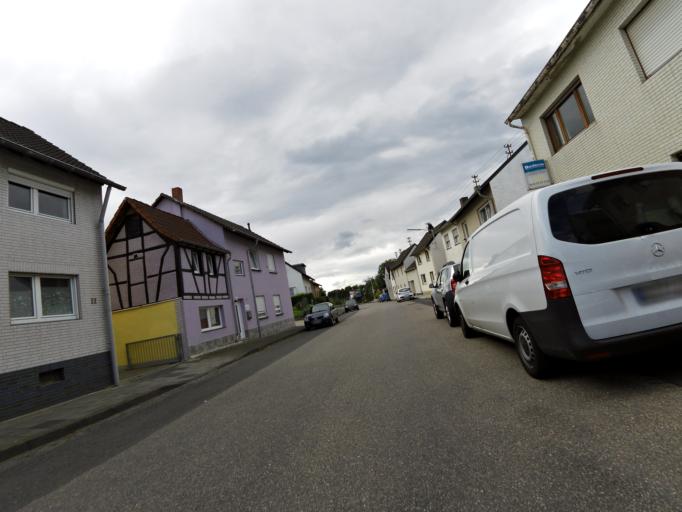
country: DE
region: North Rhine-Westphalia
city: Meckenheim
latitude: 50.5835
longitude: 7.0321
